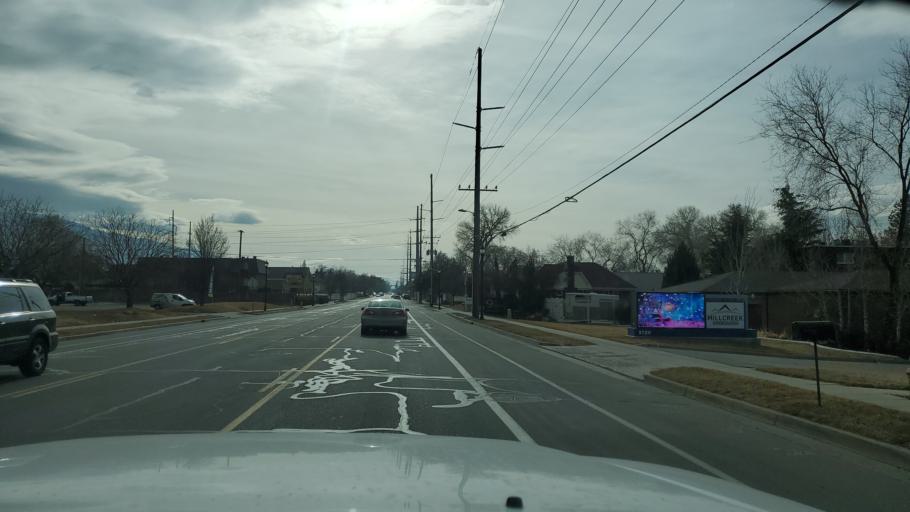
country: US
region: Utah
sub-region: Salt Lake County
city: Millcreek
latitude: 40.6910
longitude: -111.8655
